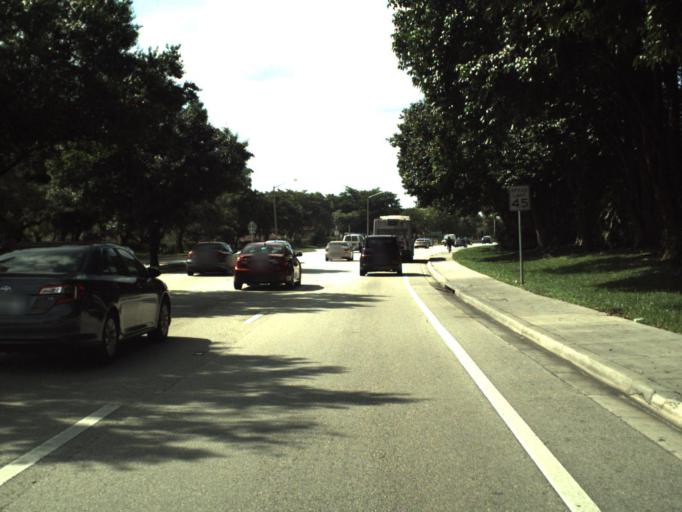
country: US
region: Florida
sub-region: Broward County
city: Tamarac
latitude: 26.2354
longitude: -80.2541
